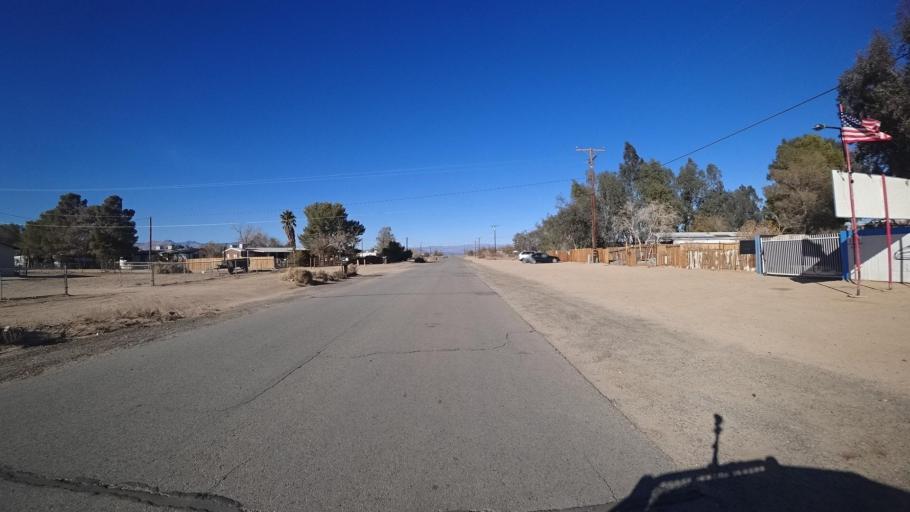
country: US
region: California
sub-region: Kern County
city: China Lake Acres
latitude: 35.6459
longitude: -117.7586
